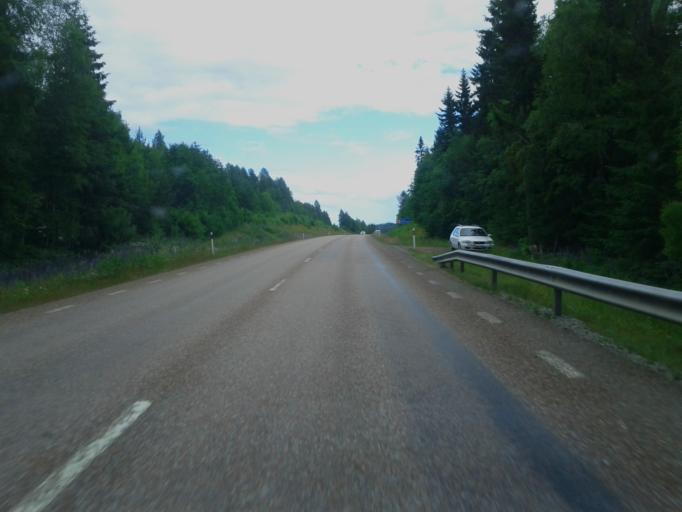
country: SE
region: Dalarna
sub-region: Faluns Kommun
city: Bjursas
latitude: 60.7577
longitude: 15.3359
